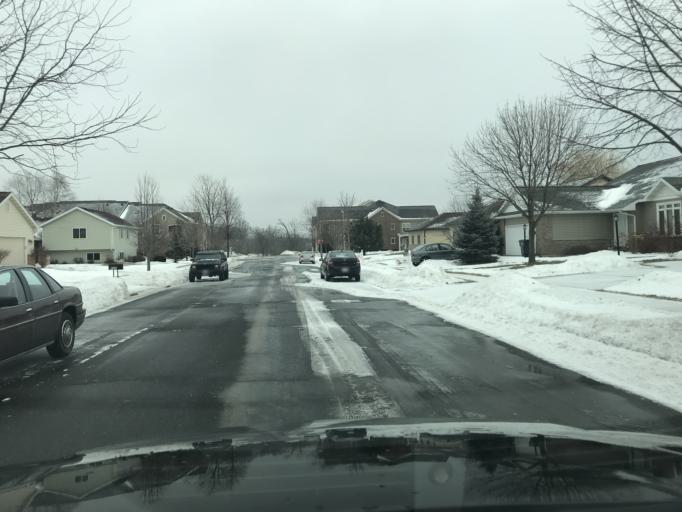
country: US
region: Wisconsin
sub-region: Dane County
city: Cottage Grove
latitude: 43.0899
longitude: -89.2162
